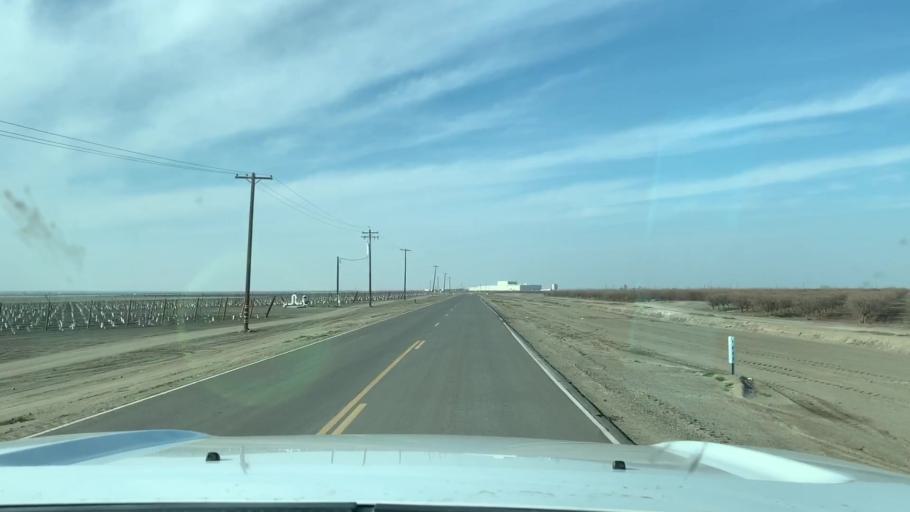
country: US
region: California
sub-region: Kern County
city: Buttonwillow
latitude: 35.4888
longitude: -119.5977
